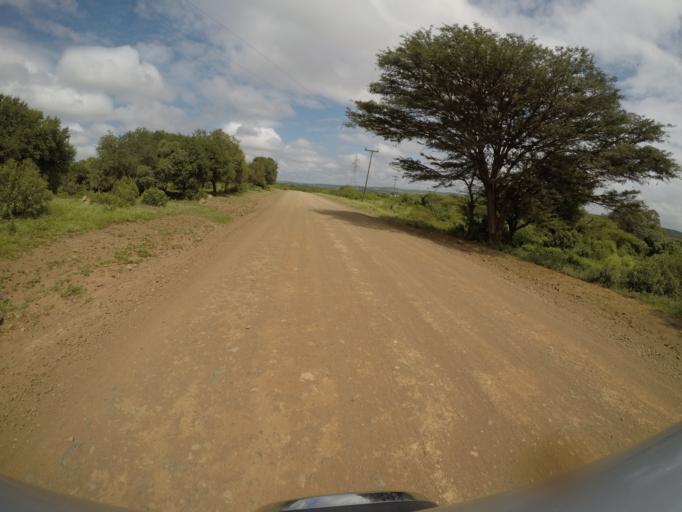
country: ZA
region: KwaZulu-Natal
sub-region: uThungulu District Municipality
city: Empangeni
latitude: -28.6214
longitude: 31.8649
